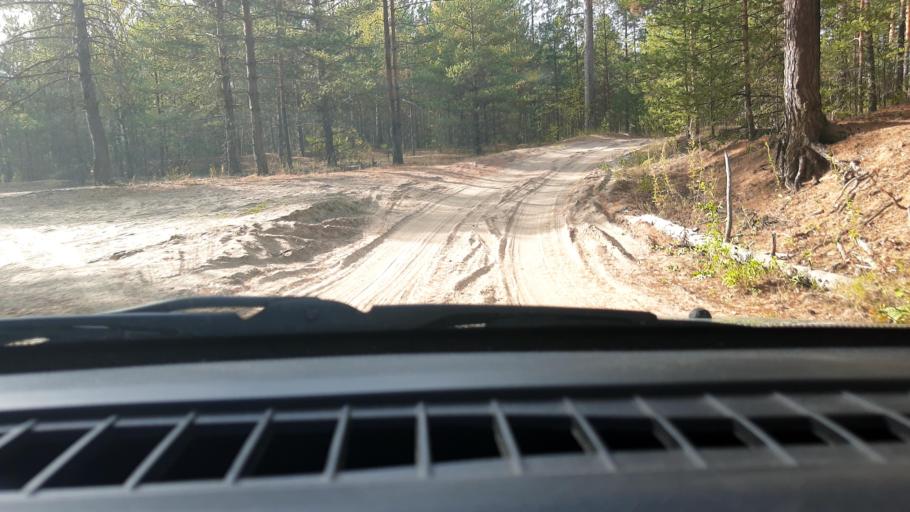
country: RU
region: Nizjnij Novgorod
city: Lukino
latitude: 56.3929
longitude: 43.6258
